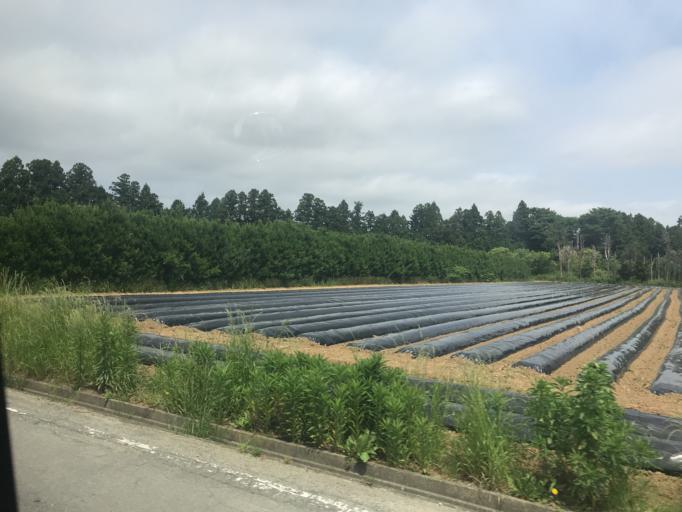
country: JP
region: Fukushima
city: Namie
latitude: 37.2962
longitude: 141.0049
